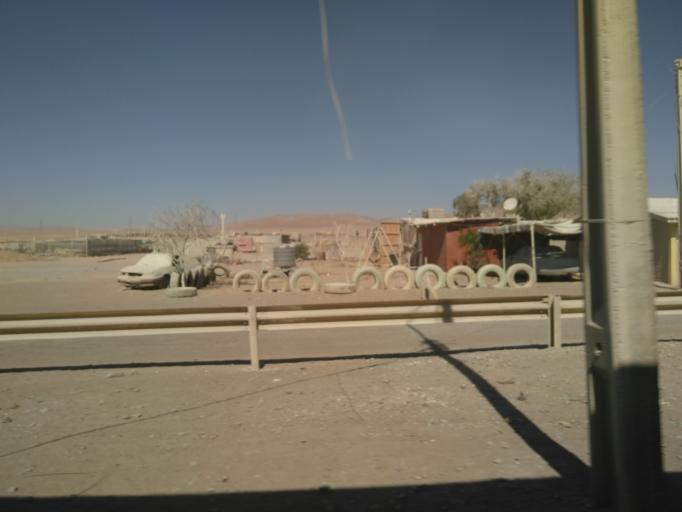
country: CL
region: Antofagasta
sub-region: Provincia de Antofagasta
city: Antofagasta
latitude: -23.7873
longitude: -70.3168
